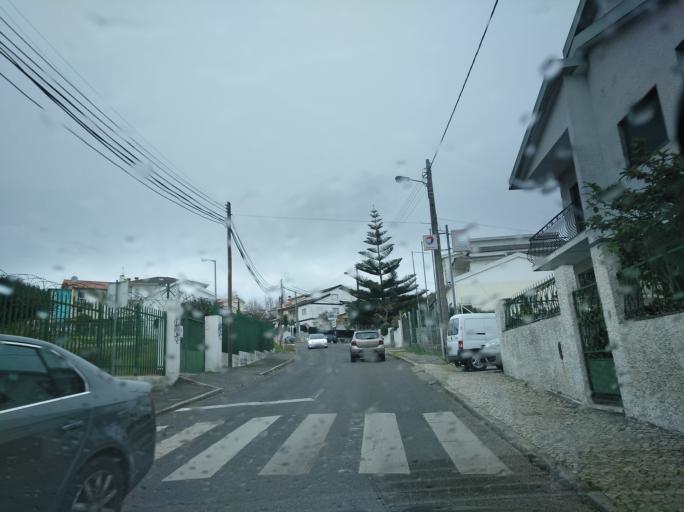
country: PT
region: Lisbon
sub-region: Odivelas
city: Famoes
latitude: 38.7931
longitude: -9.2110
